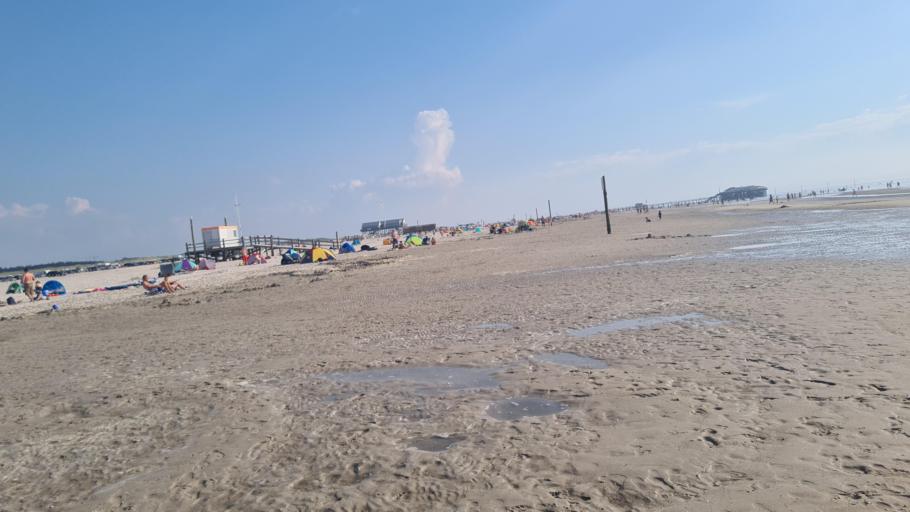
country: DE
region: Schleswig-Holstein
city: Sankt Peter-Ording
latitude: 54.3347
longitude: 8.5912
